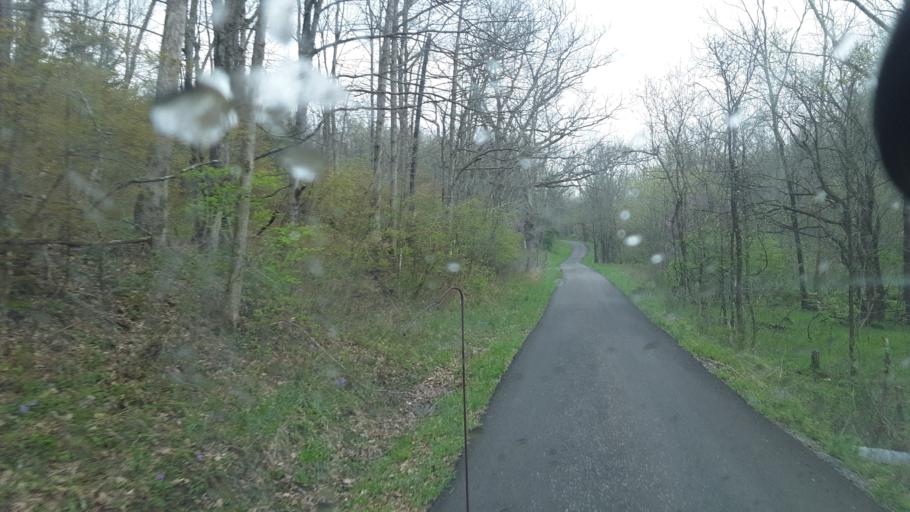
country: US
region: Kentucky
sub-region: Owen County
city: Owenton
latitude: 38.6531
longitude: -84.7868
